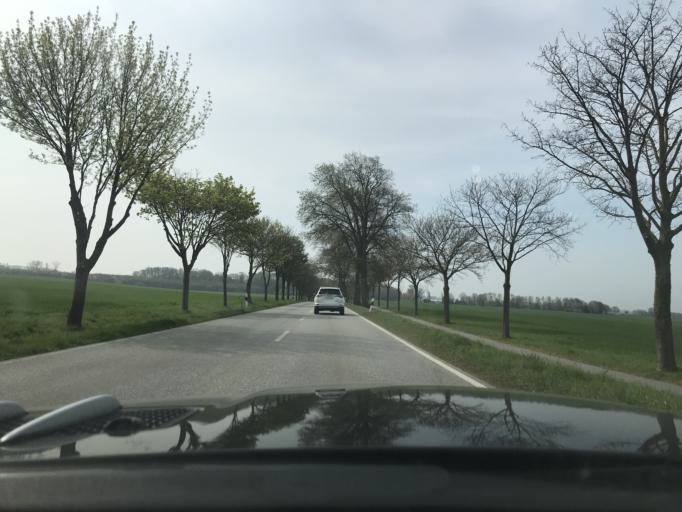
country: DE
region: Schleswig-Holstein
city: Grube
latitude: 54.2603
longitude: 11.0336
